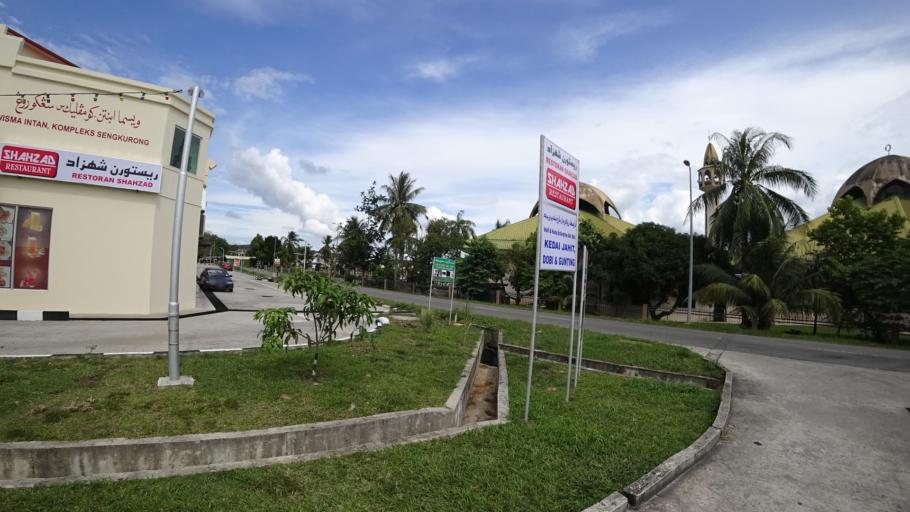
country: BN
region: Brunei and Muara
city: Bandar Seri Begawan
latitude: 4.8888
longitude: 114.8417
